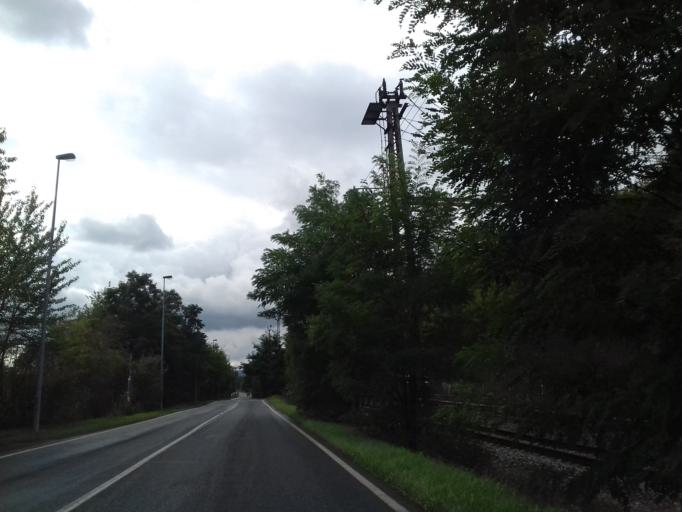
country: CZ
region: Praha
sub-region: Praha 12
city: Modrany
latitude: 49.9930
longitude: 14.3738
